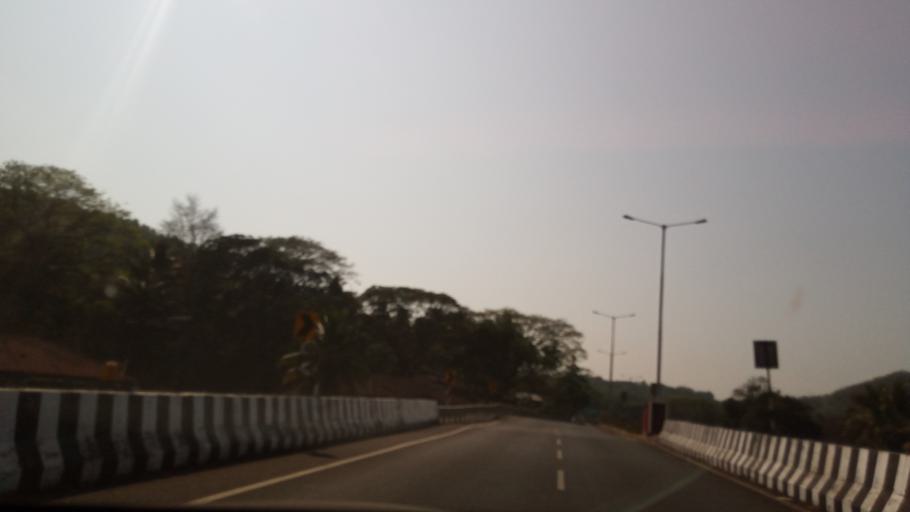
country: IN
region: Goa
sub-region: North Goa
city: Ponda
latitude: 15.4053
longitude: 74.0030
